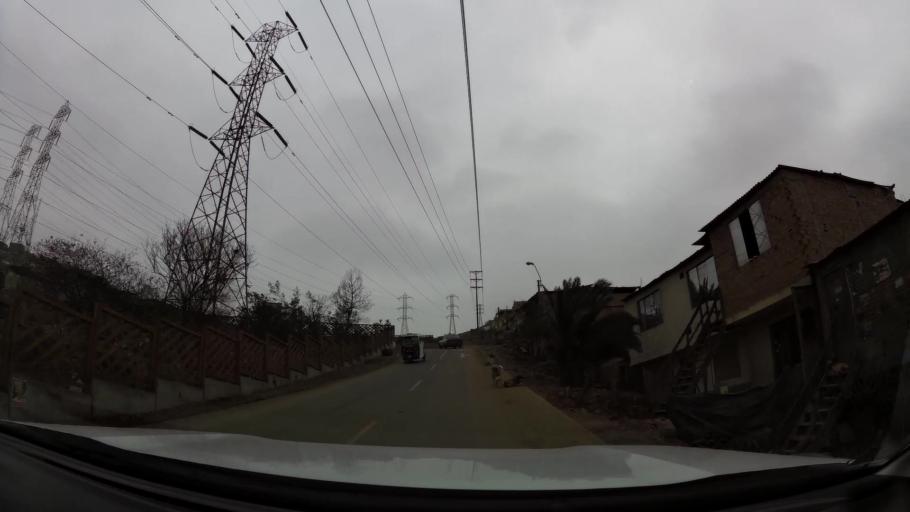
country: PE
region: Lima
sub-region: Lima
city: Surco
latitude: -12.1825
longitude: -76.9507
